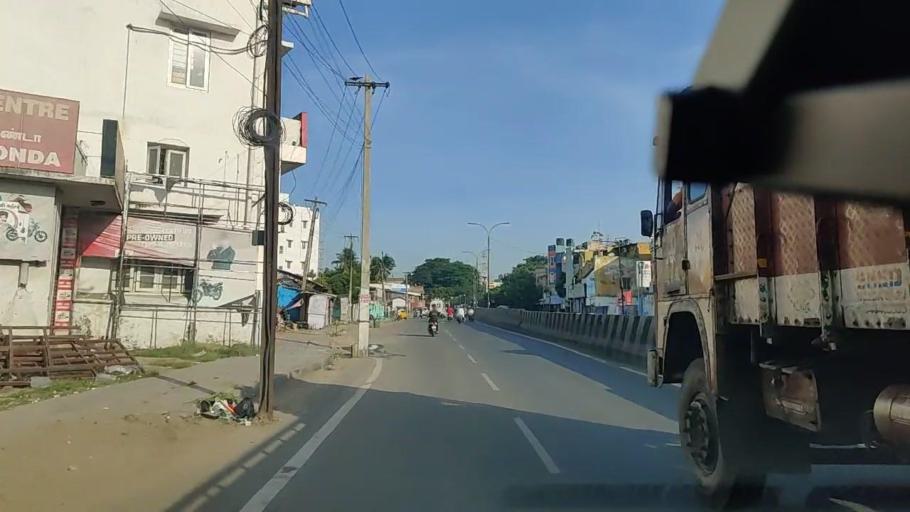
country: IN
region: Tamil Nadu
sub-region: Thiruvallur
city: Chinnasekkadu
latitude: 13.1242
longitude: 80.2476
